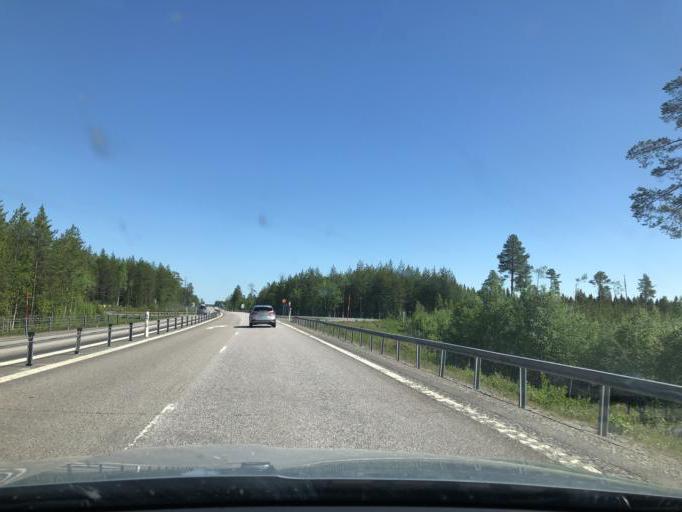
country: SE
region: Norrbotten
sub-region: Kalix Kommun
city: Toere
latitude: 65.8818
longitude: 22.5654
